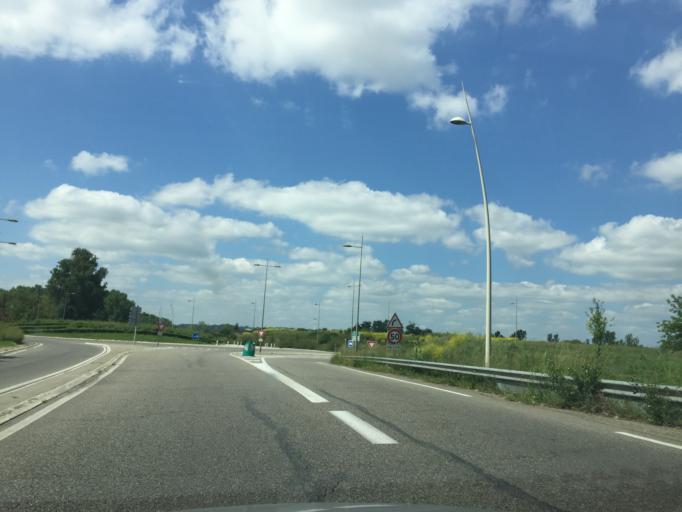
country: FR
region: Aquitaine
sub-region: Departement du Lot-et-Garonne
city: Boe
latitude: 44.1741
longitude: 0.6186
